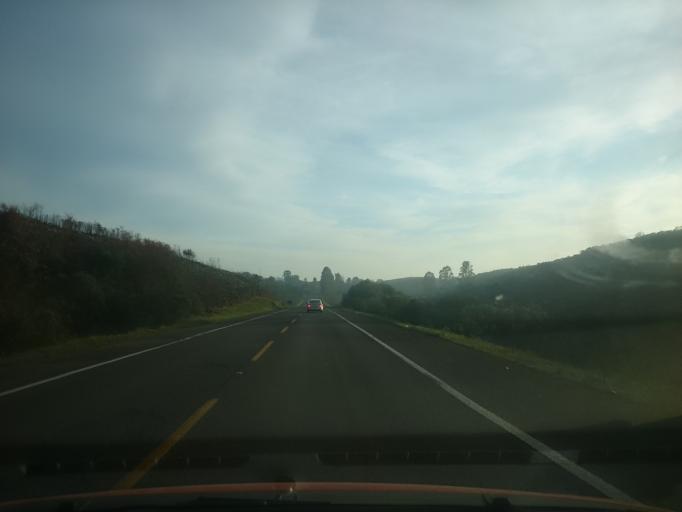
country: BR
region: Rio Grande do Sul
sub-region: Vacaria
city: Vacaria
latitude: -28.3198
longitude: -50.8050
